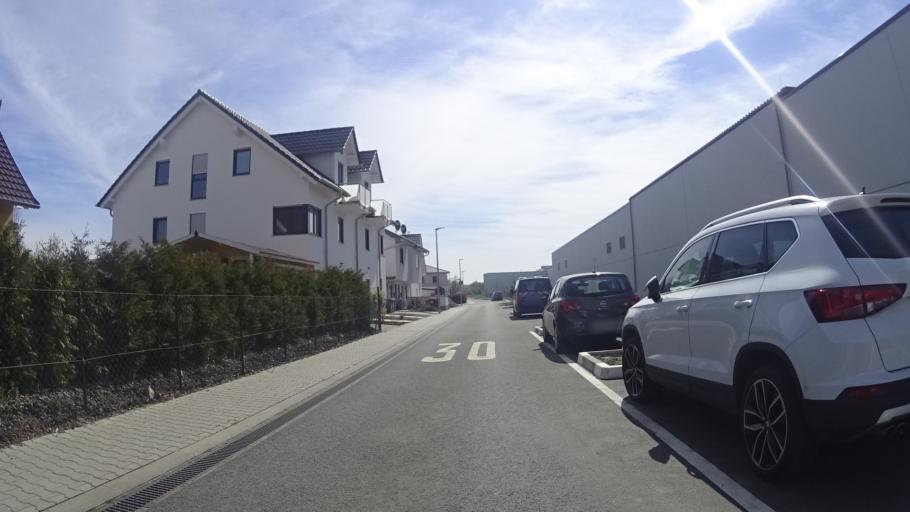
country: DE
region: Rheinland-Pfalz
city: Oppenheim
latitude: 49.8477
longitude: 8.3598
